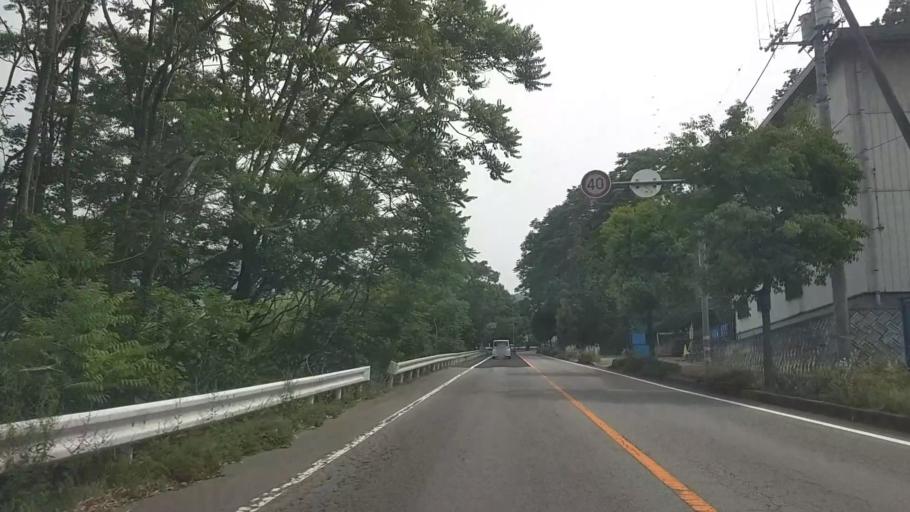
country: JP
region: Yamanashi
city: Isawa
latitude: 35.5901
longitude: 138.5903
